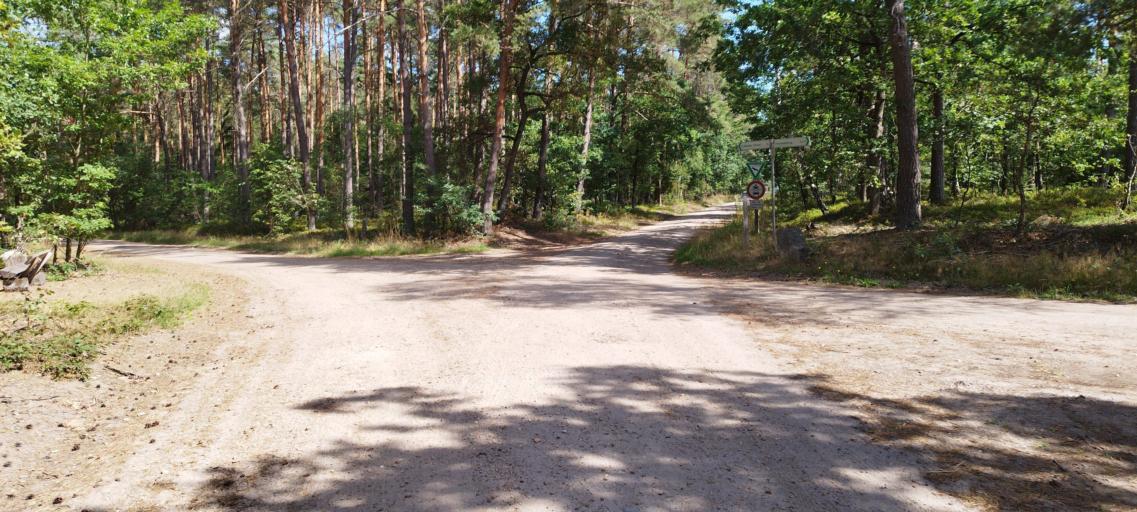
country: DE
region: Lower Saxony
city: Fassberg
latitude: 52.8642
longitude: 10.1633
